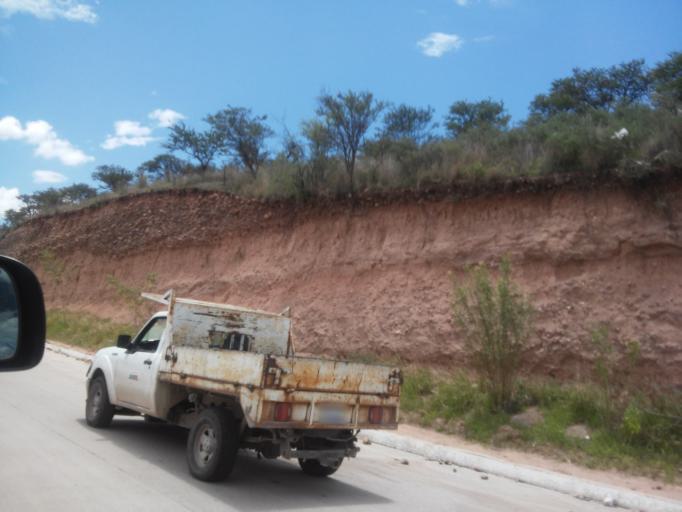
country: MX
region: Durango
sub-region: Santiago Papasquiaro
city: Santiago Papasquiaro
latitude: 25.0610
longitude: -105.4264
